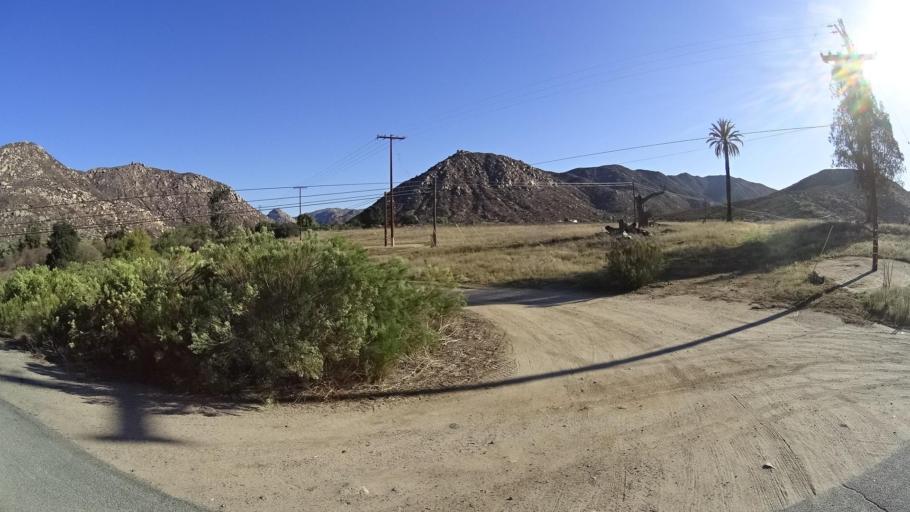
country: MX
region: Baja California
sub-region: Tecate
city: Lomas de Santa Anita
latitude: 32.6101
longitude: -116.6977
